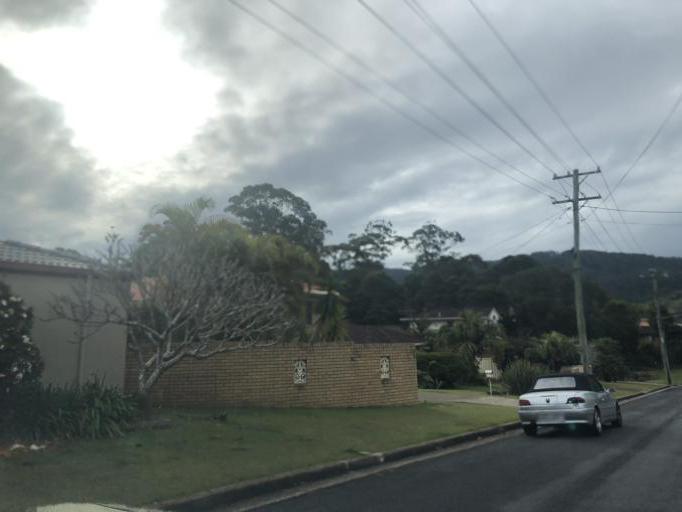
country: AU
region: New South Wales
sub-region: Coffs Harbour
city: Coffs Harbour
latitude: -30.2873
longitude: 153.1108
